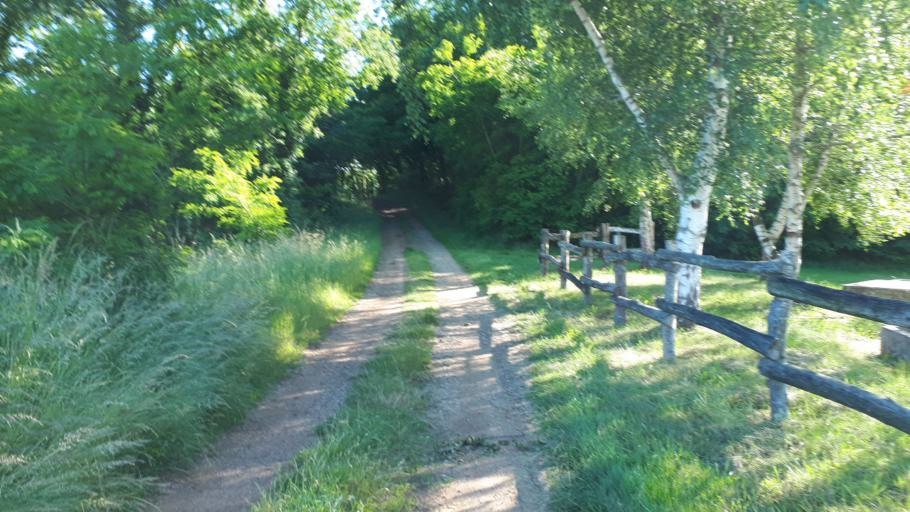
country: FR
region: Centre
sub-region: Departement du Loir-et-Cher
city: Sarge-sur-Braye
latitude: 47.9321
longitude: 0.8705
